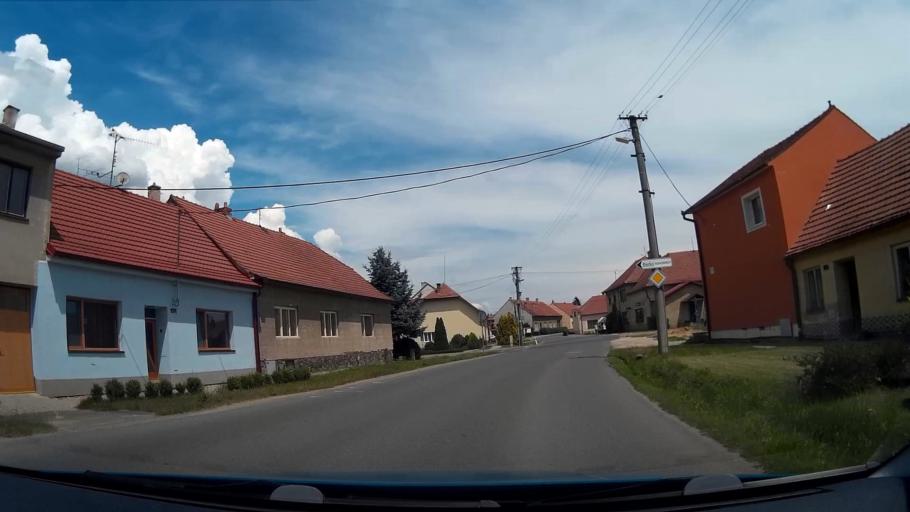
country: CZ
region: South Moravian
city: Orechov
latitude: 49.0796
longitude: 16.5457
